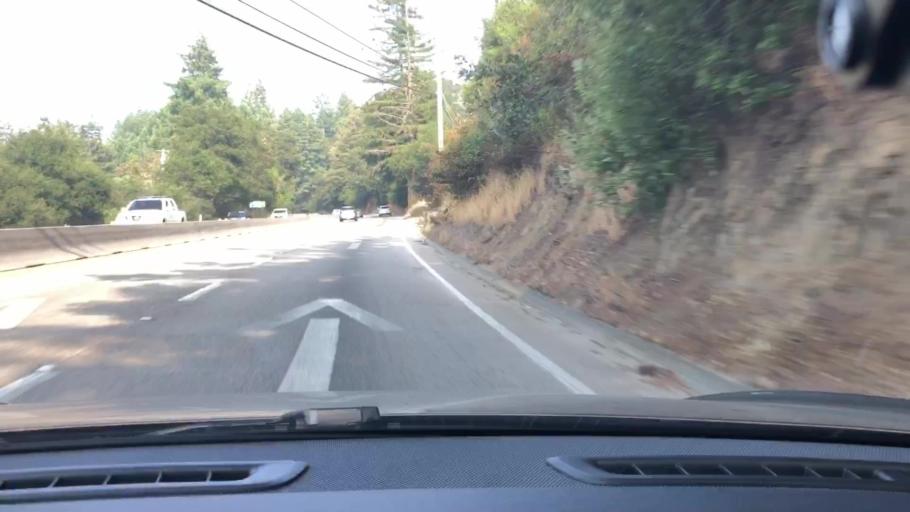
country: US
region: California
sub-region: Santa Cruz County
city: Scotts Valley
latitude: 37.0765
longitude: -121.9863
